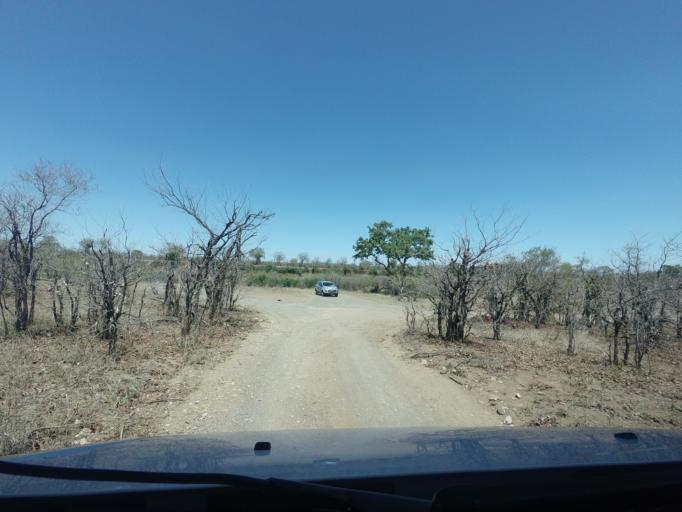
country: ZA
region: Limpopo
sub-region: Mopani District Municipality
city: Phalaborwa
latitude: -23.5845
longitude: 31.4483
